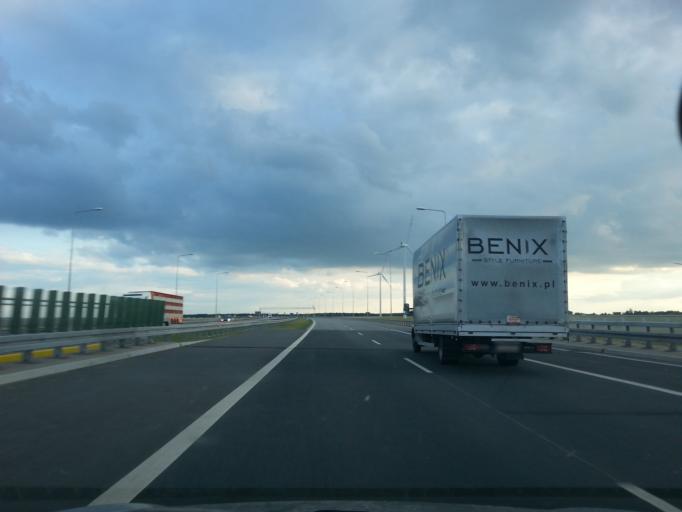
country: PL
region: Lodz Voivodeship
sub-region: Powiat sieradzki
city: Sieradz
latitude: 51.5557
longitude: 18.7156
